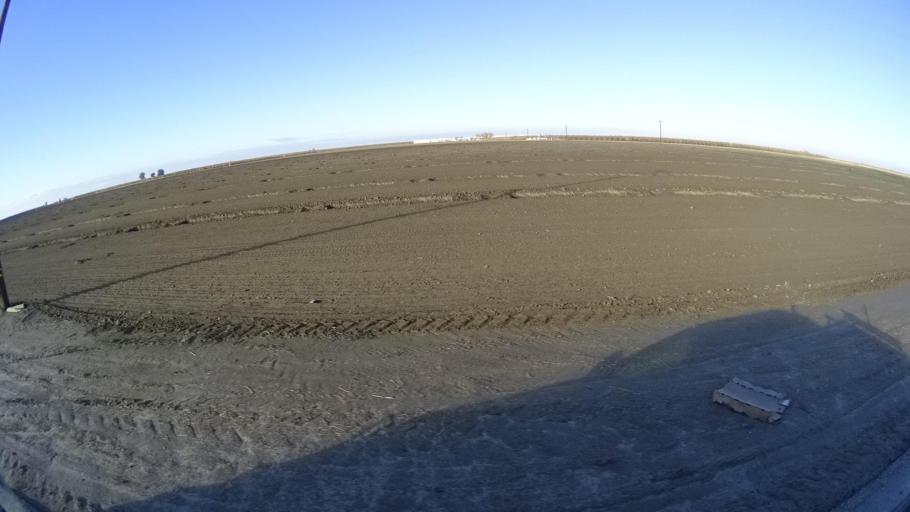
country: US
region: California
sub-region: Kern County
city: Delano
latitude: 35.7530
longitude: -119.3303
